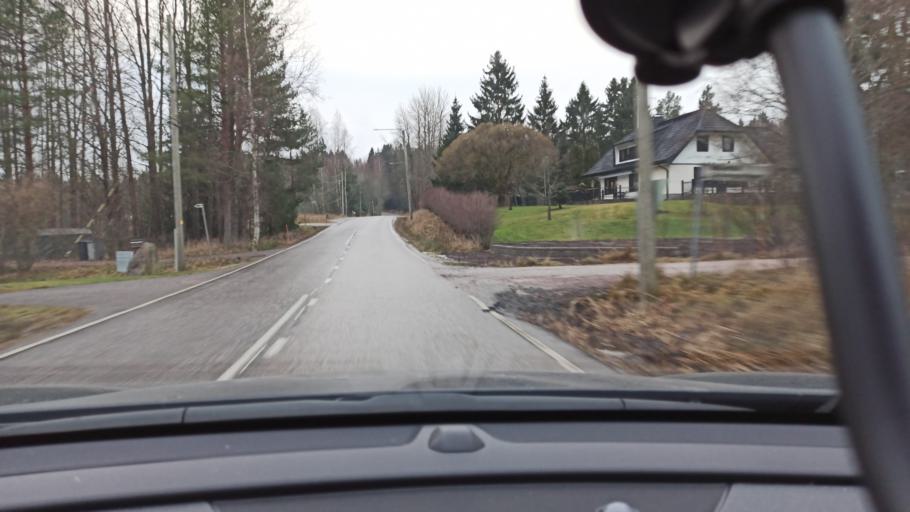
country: FI
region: Uusimaa
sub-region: Helsinki
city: Kirkkonummi
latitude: 60.1512
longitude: 24.4610
